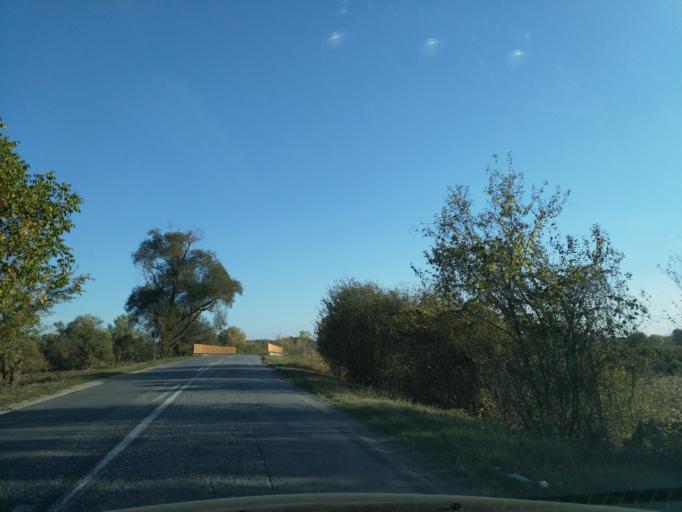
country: RS
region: Central Serbia
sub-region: Pomoravski Okrug
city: Svilajnac
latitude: 44.2295
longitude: 21.1445
